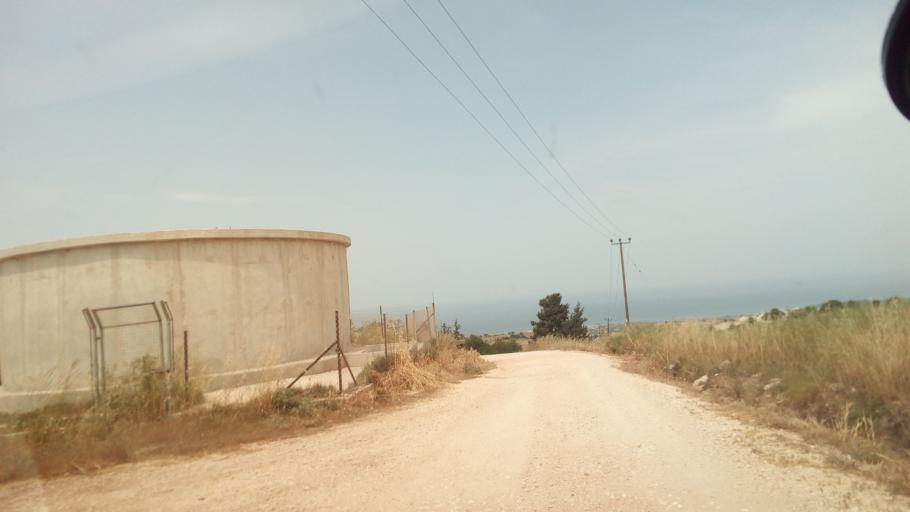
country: CY
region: Pafos
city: Polis
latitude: 34.9950
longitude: 32.3826
